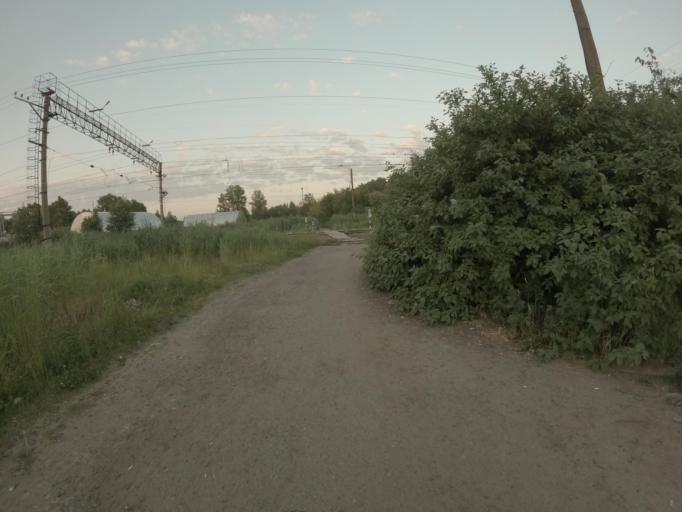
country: RU
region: St.-Petersburg
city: Avtovo
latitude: 59.8759
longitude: 30.2813
